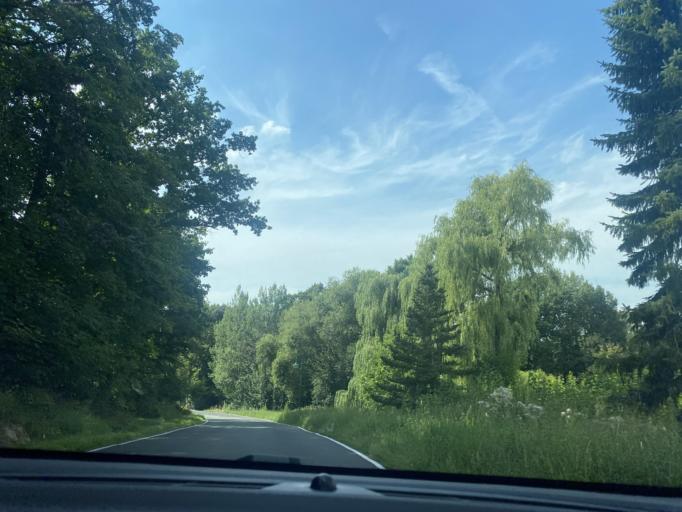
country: DE
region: Saxony
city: Sohland am Rotstein
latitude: 51.1060
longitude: 14.7865
